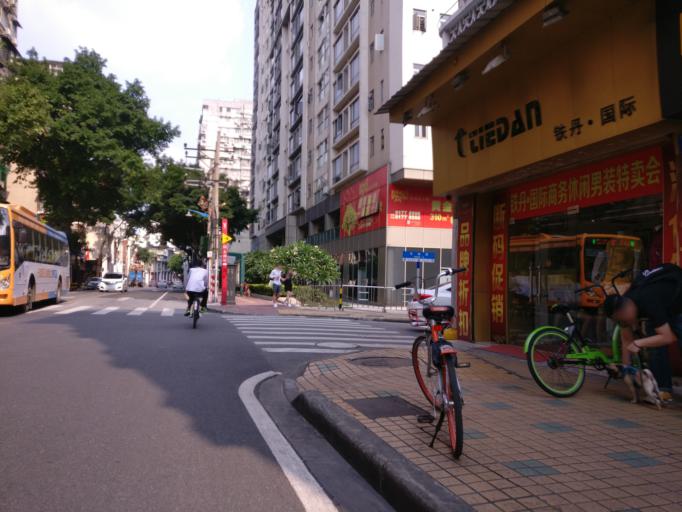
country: CN
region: Guangdong
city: Guangzhou
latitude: 23.1237
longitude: 113.2857
